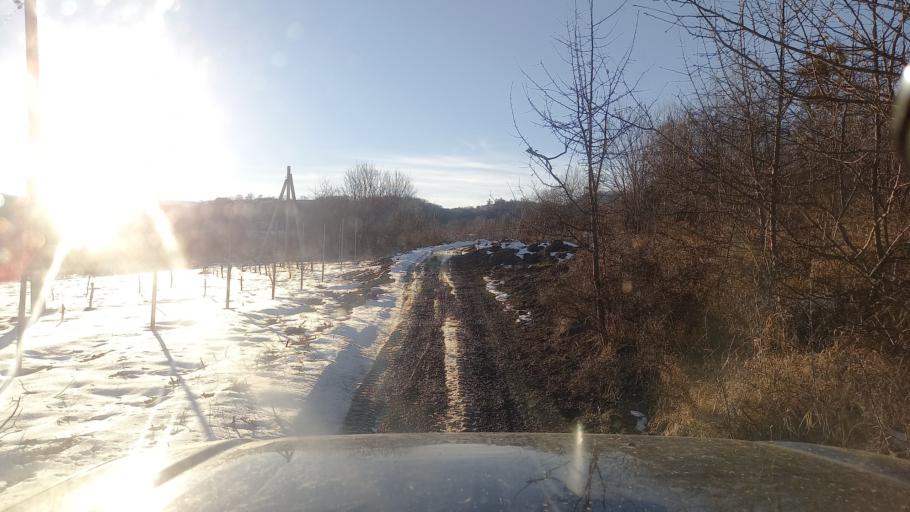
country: RU
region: Adygeya
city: Kamennomostskiy
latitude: 44.2288
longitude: 40.1684
